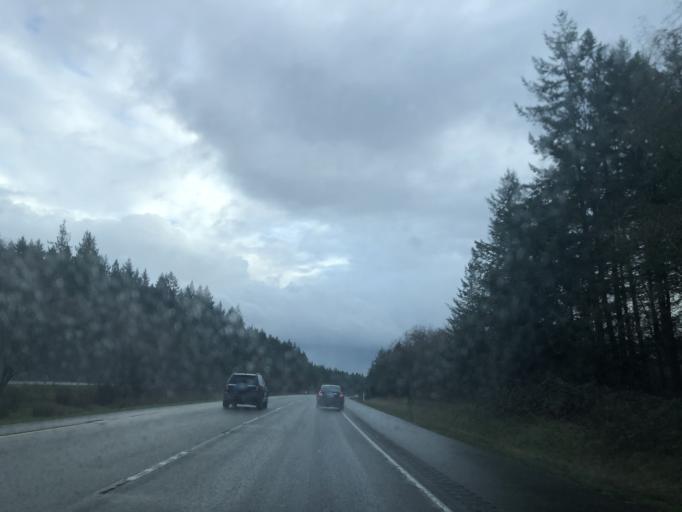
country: US
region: Washington
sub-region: Pierce County
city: Purdy
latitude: 47.3883
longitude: -122.6164
